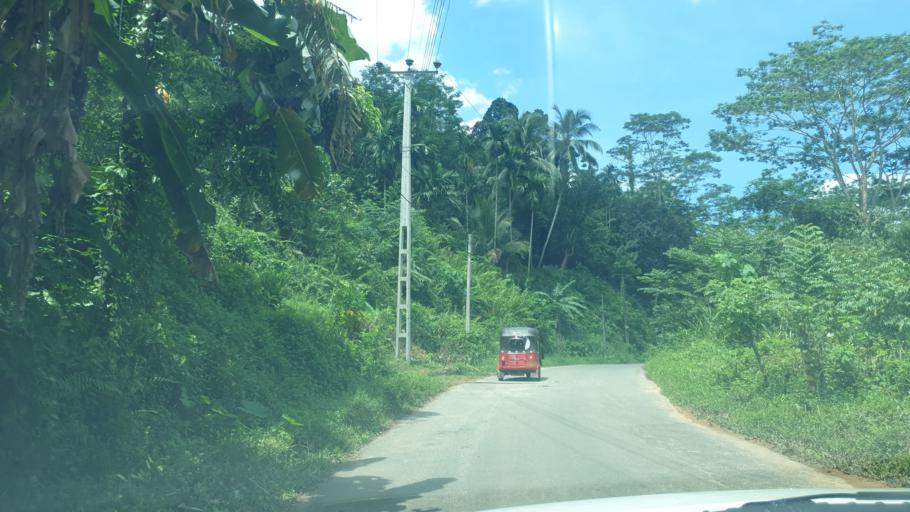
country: LK
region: Sabaragamuwa
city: Ratnapura
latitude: 6.4838
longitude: 80.4085
